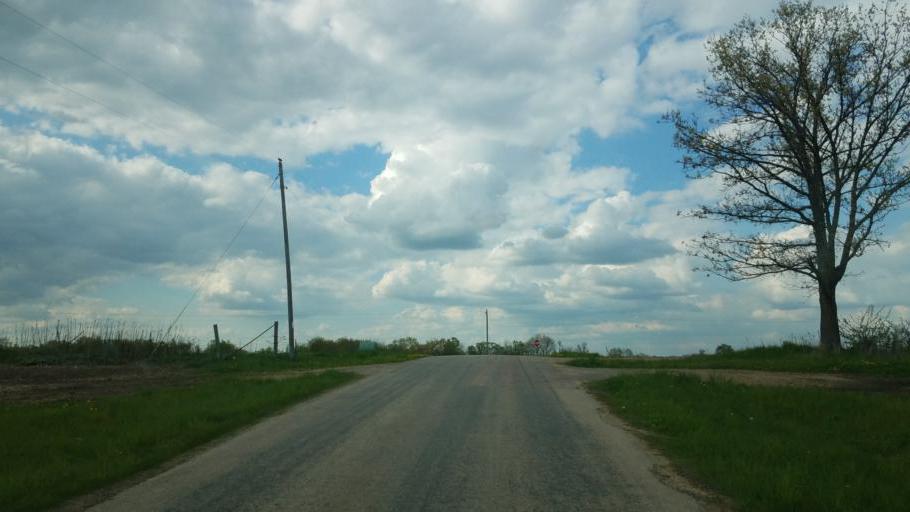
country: US
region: Wisconsin
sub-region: Vernon County
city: Hillsboro
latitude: 43.5903
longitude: -90.3318
